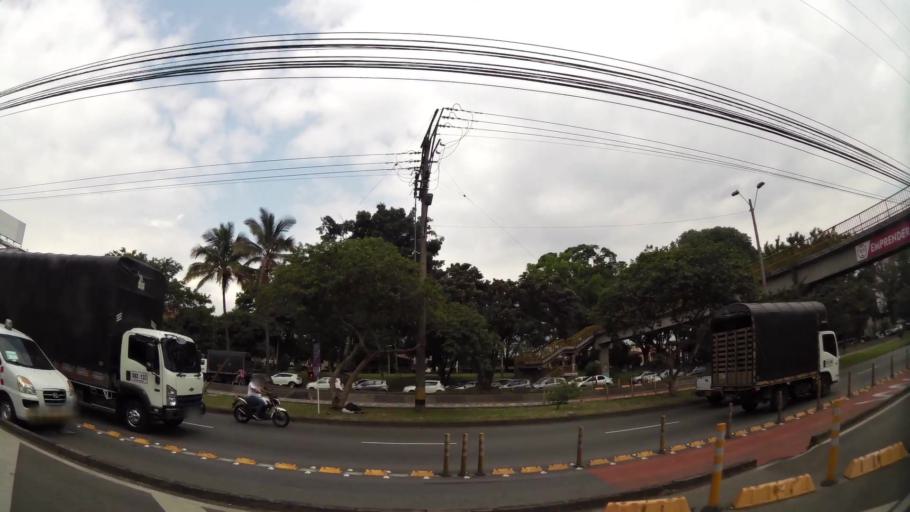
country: CO
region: Antioquia
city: Medellin
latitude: 6.2199
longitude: -75.5801
